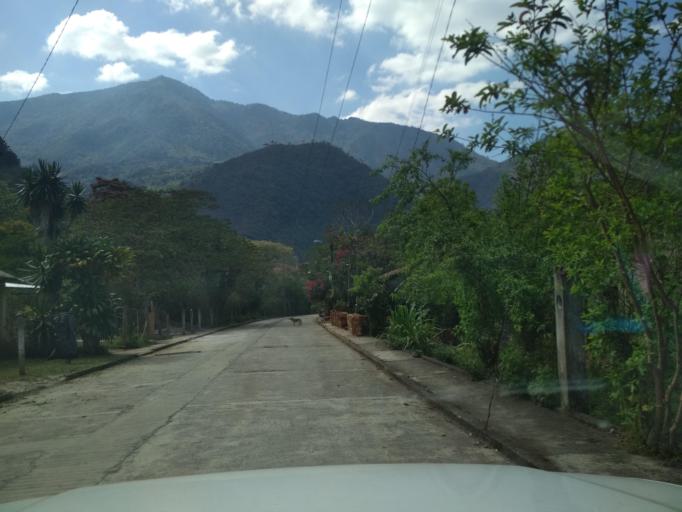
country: MX
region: Veracruz
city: Jalapilla
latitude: 18.7902
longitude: -97.0983
